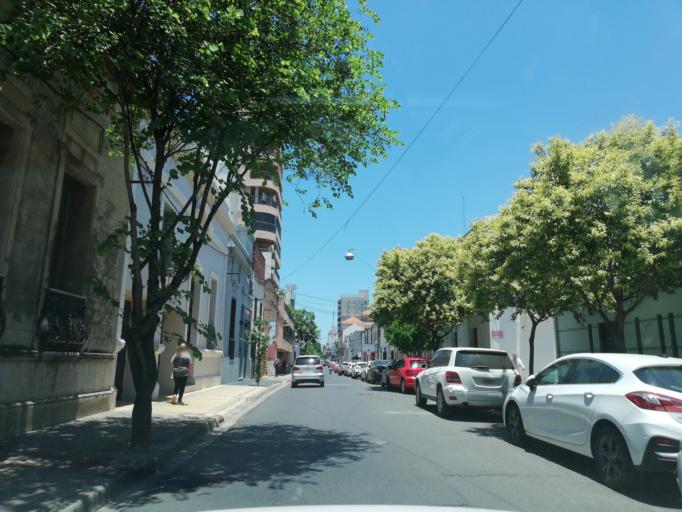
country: AR
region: Corrientes
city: Corrientes
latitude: -27.4638
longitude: -58.8313
